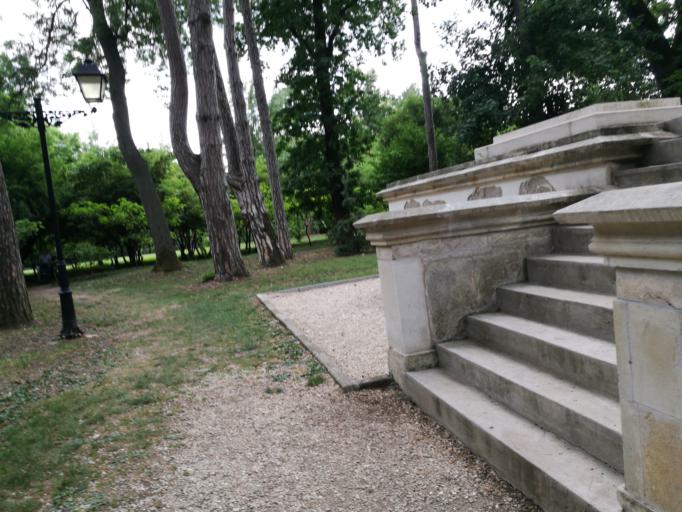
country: RO
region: Ilfov
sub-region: Comuna Mogosoaia
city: Mogosoaia
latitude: 44.5263
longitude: 25.9931
